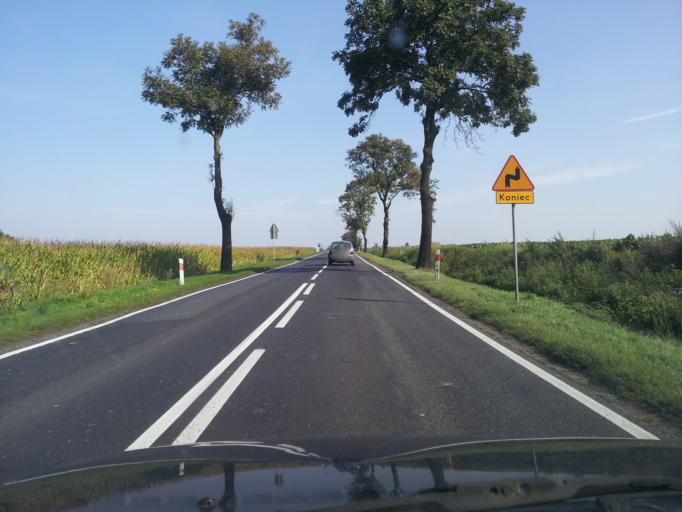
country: PL
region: Kujawsko-Pomorskie
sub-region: Powiat mogilenski
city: Mogilno
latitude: 52.6131
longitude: 17.9175
